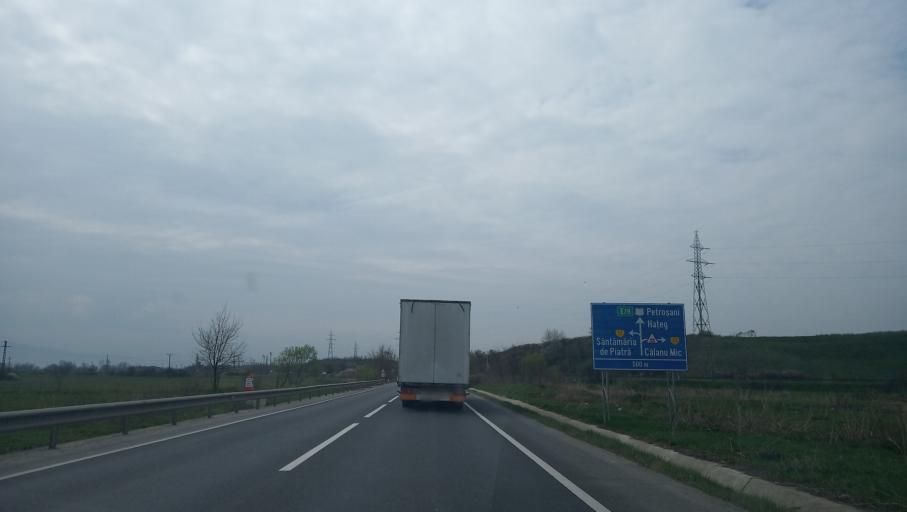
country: RO
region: Hunedoara
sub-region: Comuna Bacia
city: Bacia
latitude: 45.7703
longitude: 23.0008
